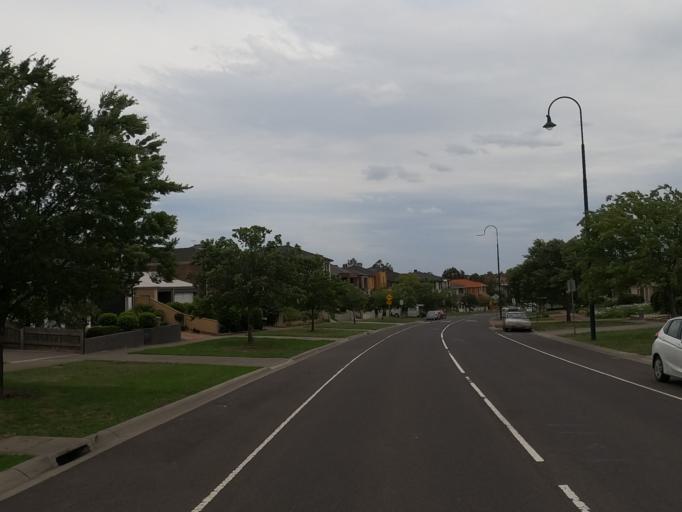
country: AU
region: Victoria
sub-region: Hume
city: Meadow Heights
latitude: -37.6419
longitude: 144.9082
